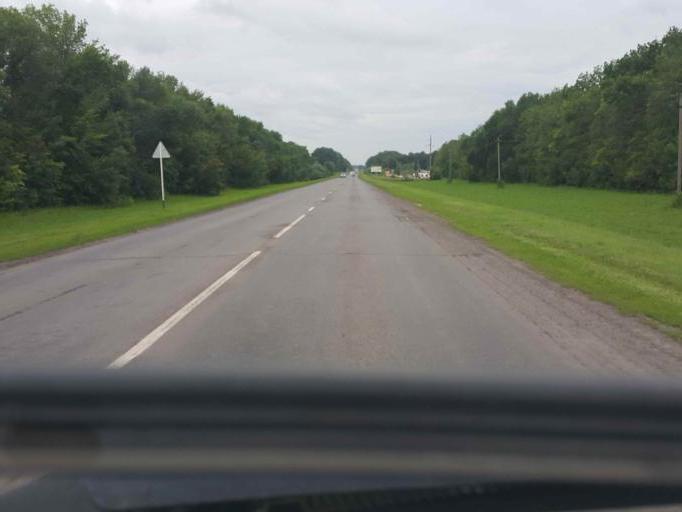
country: RU
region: Tambov
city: Zavoronezhskoye
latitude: 52.9036
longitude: 40.6128
